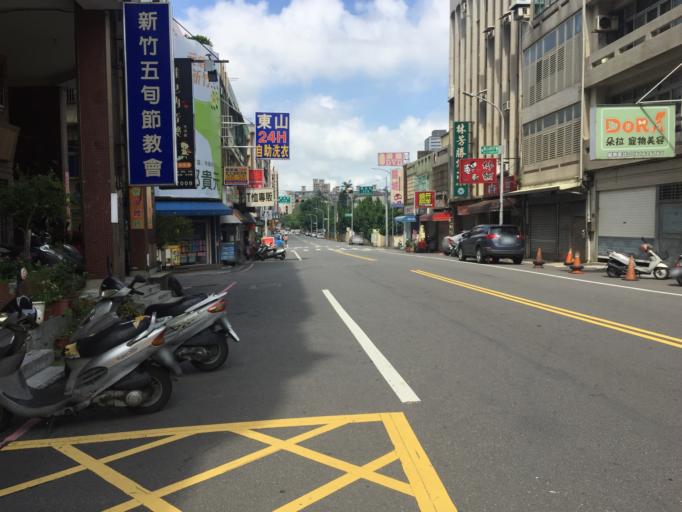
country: TW
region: Taiwan
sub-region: Hsinchu
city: Hsinchu
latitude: 24.7963
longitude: 120.9799
